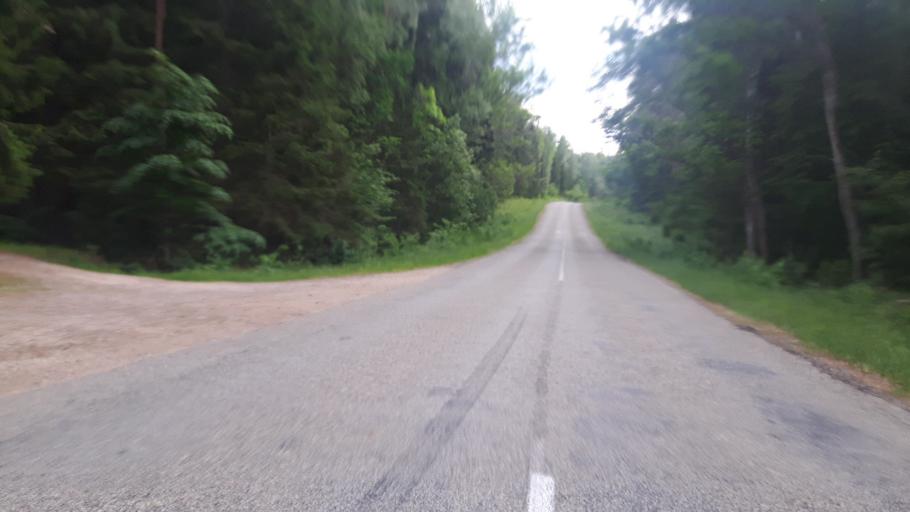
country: LV
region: Engure
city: Smarde
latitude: 57.0007
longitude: 23.3289
